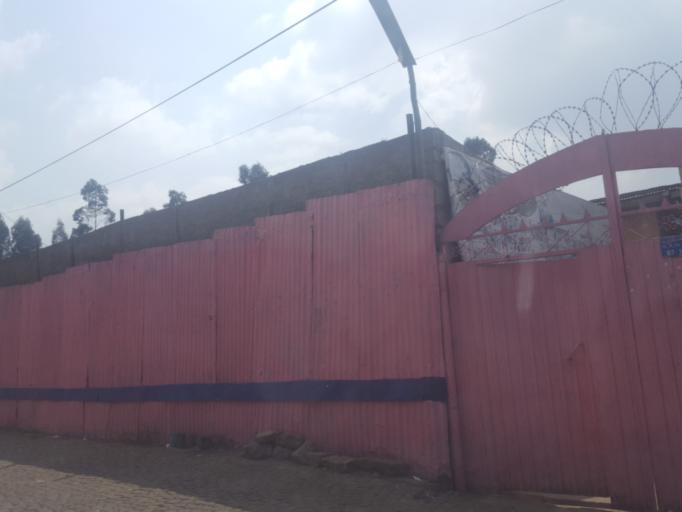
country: ET
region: Adis Abeba
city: Addis Ababa
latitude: 9.0639
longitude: 38.7252
